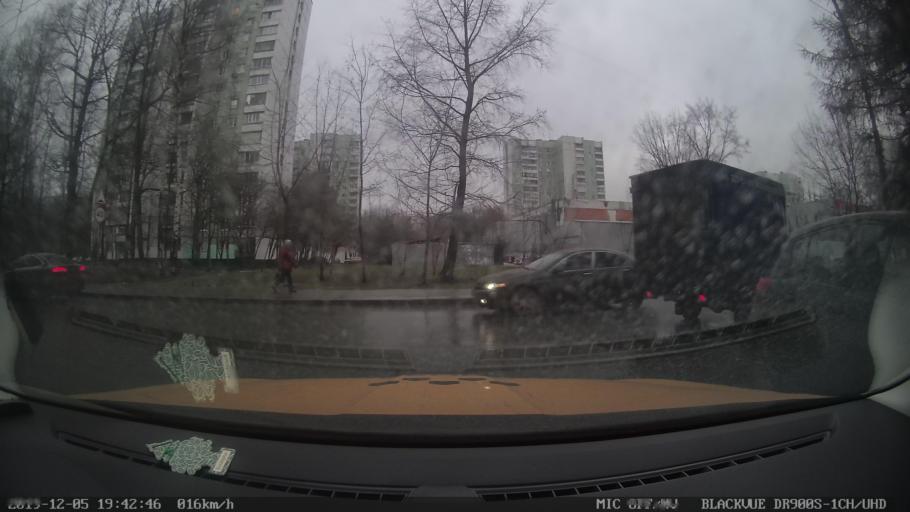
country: RU
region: Moscow
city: Lianozovo
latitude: 55.8972
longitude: 37.5803
